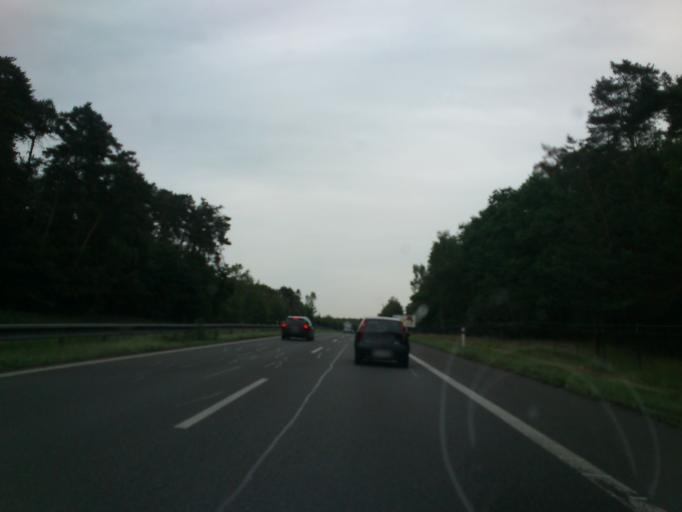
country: CZ
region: Central Bohemia
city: Brandys nad Labem-Stara Boleslav
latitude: 50.2088
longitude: 14.6977
